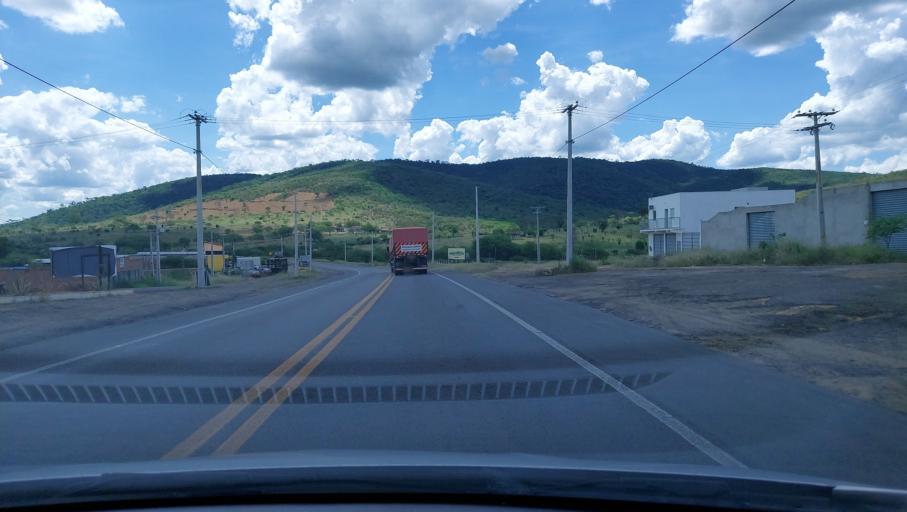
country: BR
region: Bahia
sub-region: Itaberaba
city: Itaberaba
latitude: -12.5117
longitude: -40.3257
